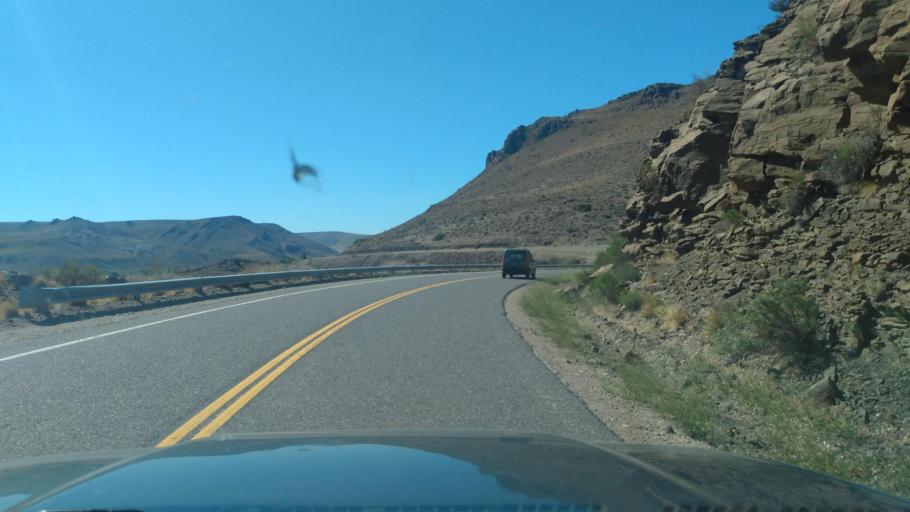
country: AR
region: Neuquen
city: Junin de los Andes
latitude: -40.0529
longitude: -70.8141
